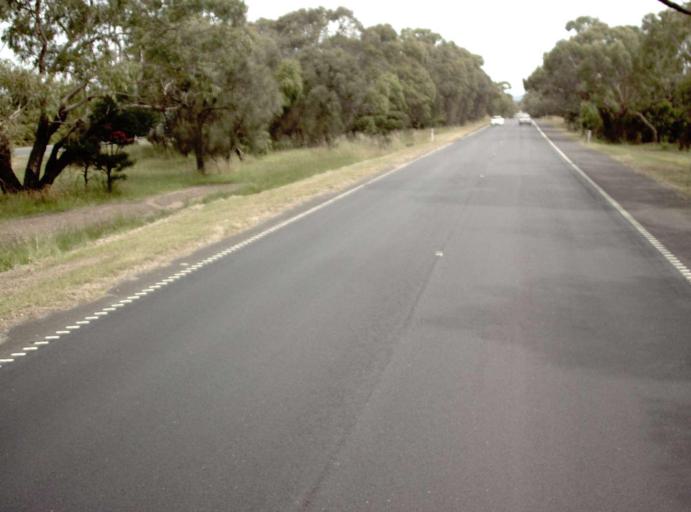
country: AU
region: Victoria
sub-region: Mornington Peninsula
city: Moorooduc
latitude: -38.2474
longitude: 145.0829
